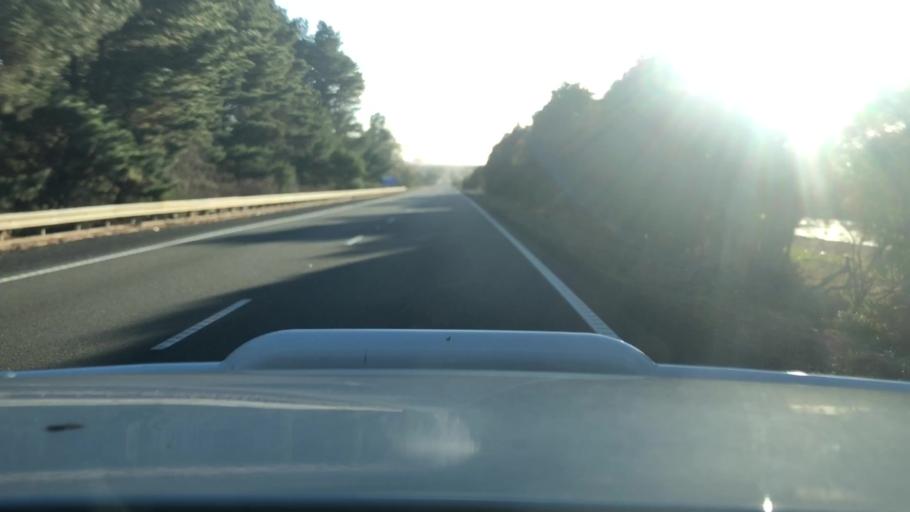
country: AU
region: New South Wales
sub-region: Wingecarribee
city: Moss Vale
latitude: -34.5519
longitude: 150.2669
